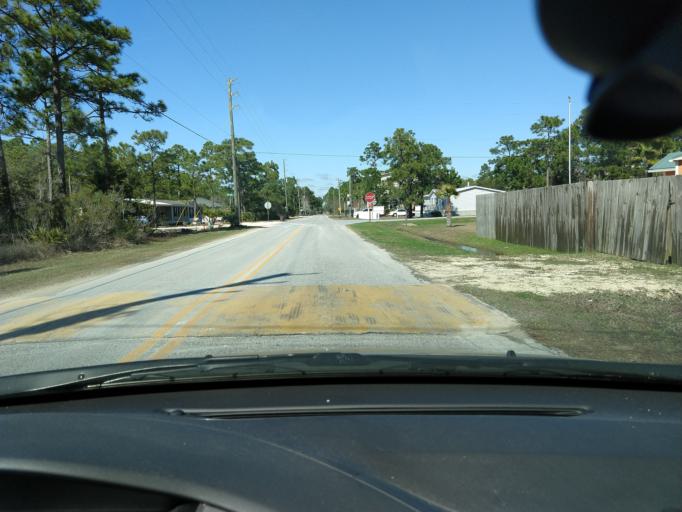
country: US
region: Florida
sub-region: Walton County
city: Miramar Beach
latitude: 30.3921
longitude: -86.3002
